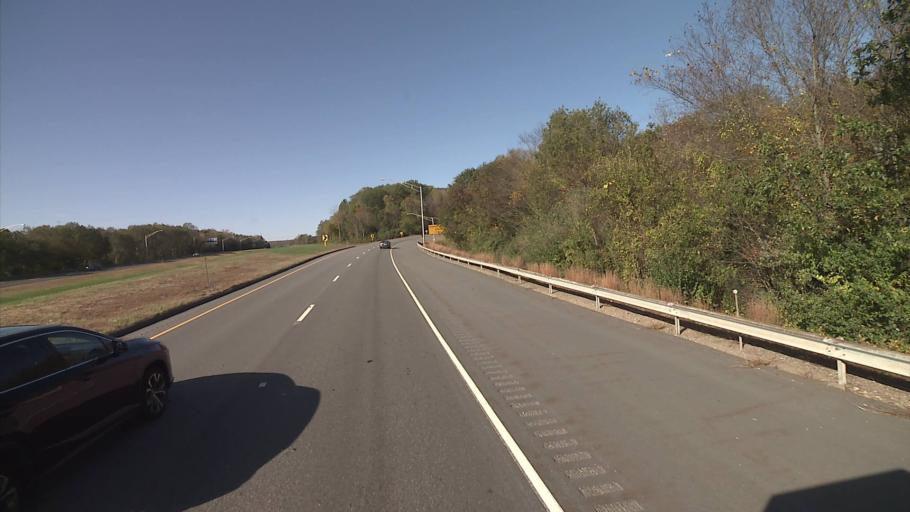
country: US
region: Connecticut
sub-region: Tolland County
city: Mansfield City
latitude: 41.7234
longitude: -72.2599
